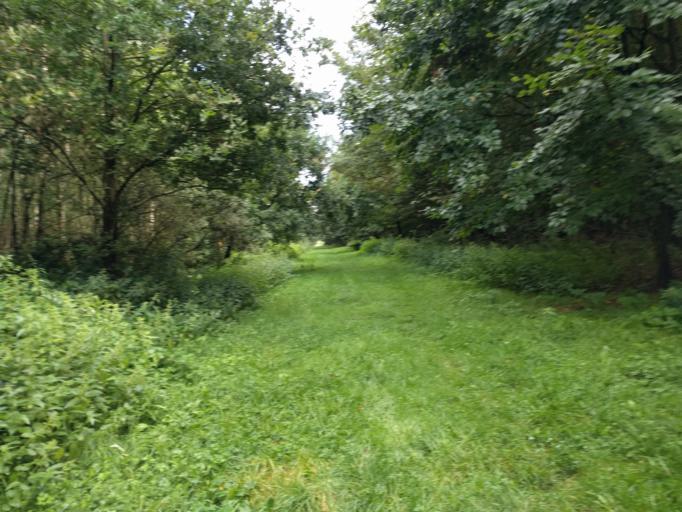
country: BE
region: Flanders
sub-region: Provincie West-Vlaanderen
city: Lendelede
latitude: 50.8765
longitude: 3.2439
